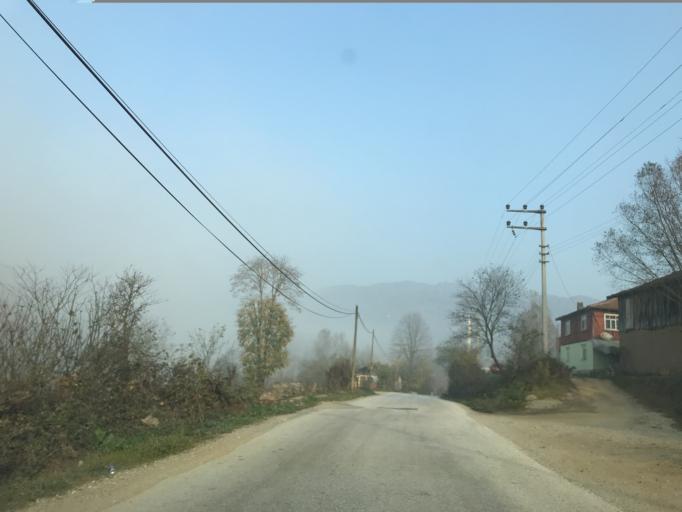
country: TR
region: Duzce
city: Cumayeri
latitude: 40.9056
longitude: 30.9511
